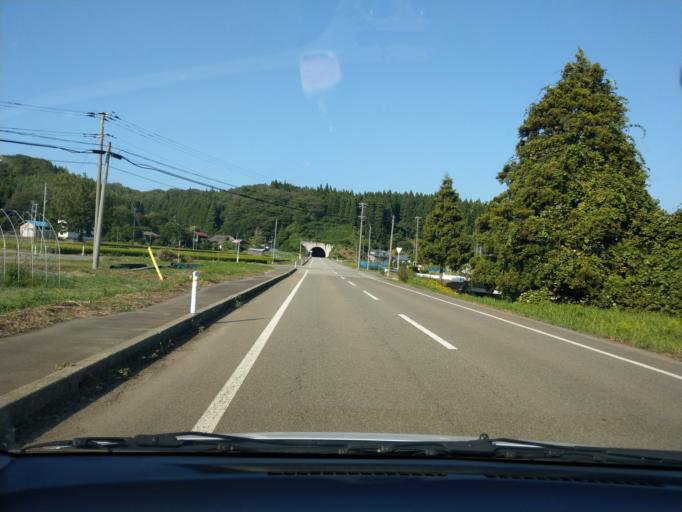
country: JP
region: Akita
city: Akita
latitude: 39.6007
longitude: 140.2166
